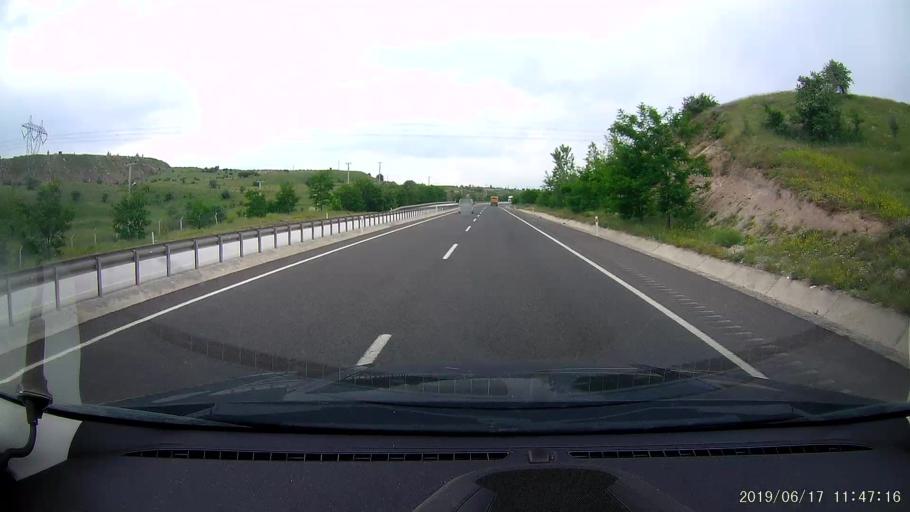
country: TR
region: Cankiri
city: Kursunlu
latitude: 40.8437
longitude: 33.2099
